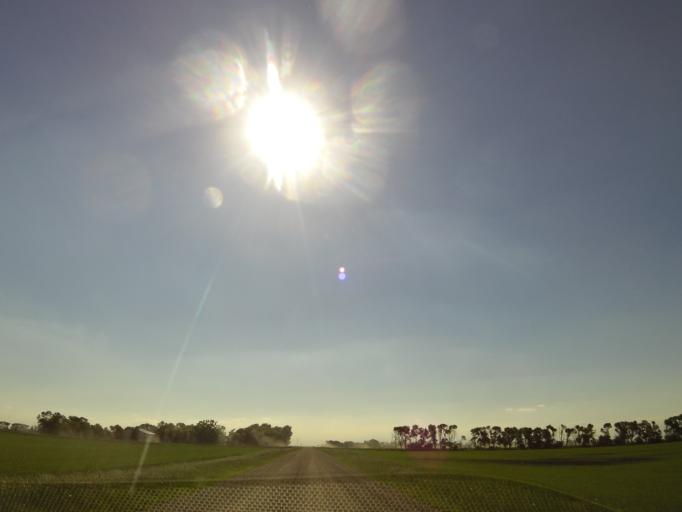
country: US
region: North Dakota
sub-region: Walsh County
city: Grafton
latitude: 48.3535
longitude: -97.2514
